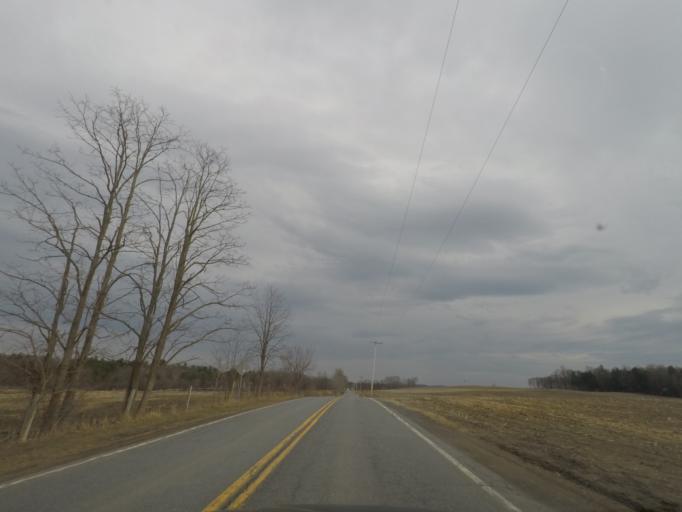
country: US
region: New York
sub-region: Washington County
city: Cambridge
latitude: 42.9629
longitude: -73.4603
